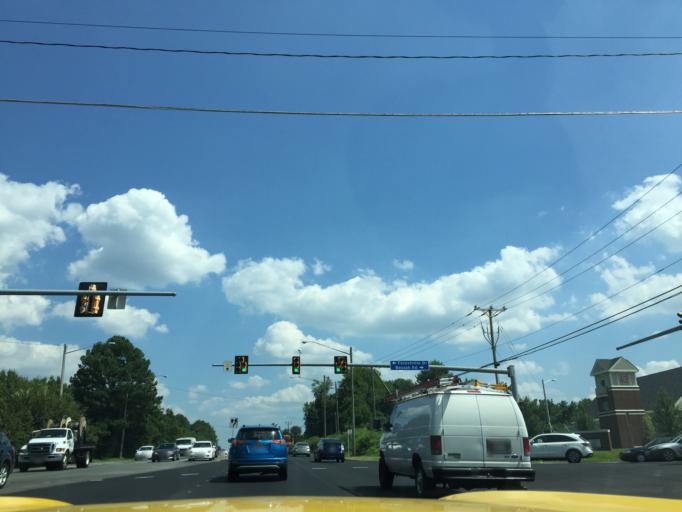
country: US
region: Virginia
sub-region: Fairfax County
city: Wolf Trap
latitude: 38.9582
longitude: -77.2751
